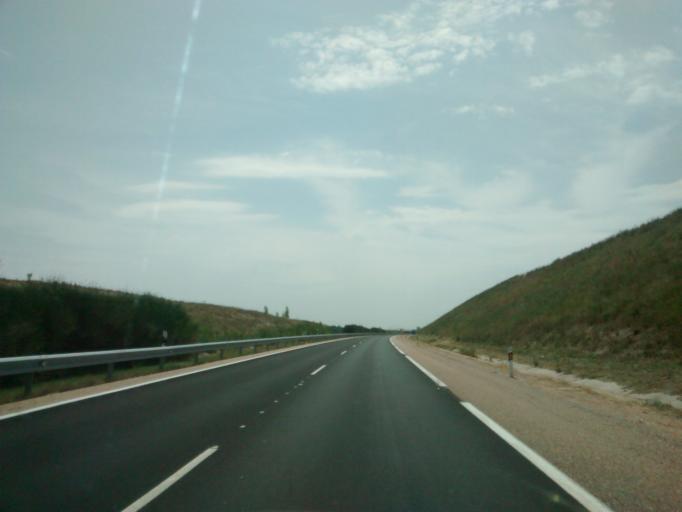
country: ES
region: Castille and Leon
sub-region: Provincia de Burgos
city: Villalbilla de Burgos
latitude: 42.3284
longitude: -3.7732
